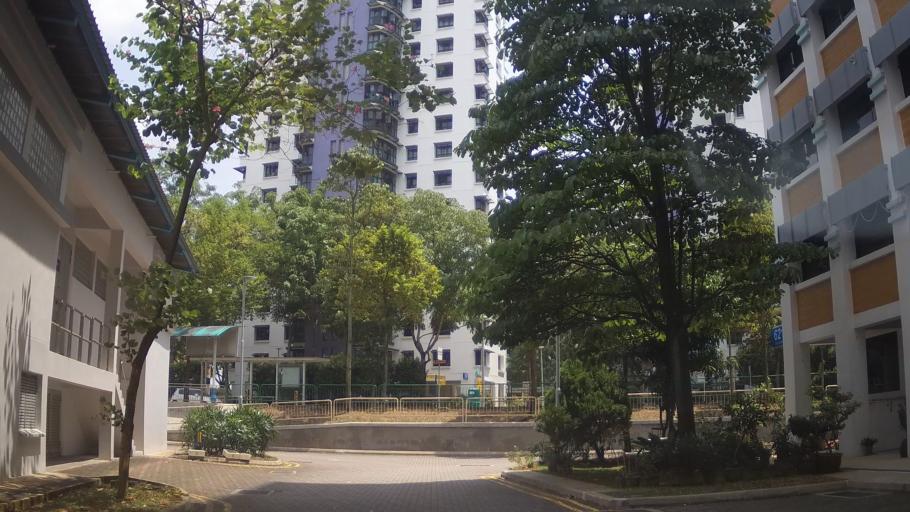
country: MY
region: Johor
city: Johor Bahru
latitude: 1.3863
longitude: 103.7629
